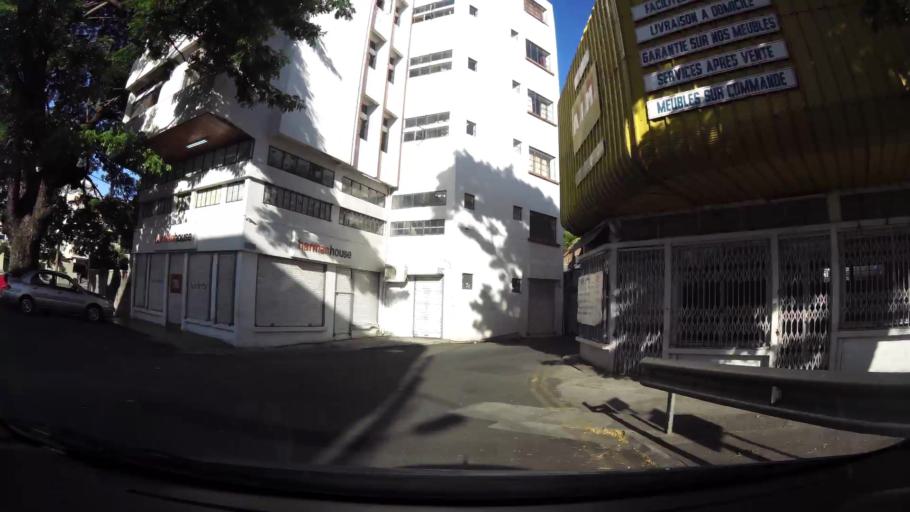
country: MU
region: Port Louis
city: Port Louis
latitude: -20.1654
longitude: 57.4951
